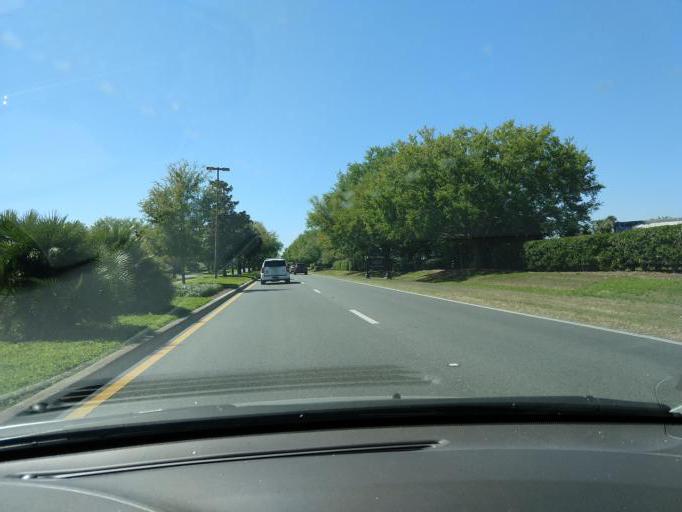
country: US
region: Florida
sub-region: Sumter County
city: The Villages
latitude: 28.9529
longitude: -81.9661
